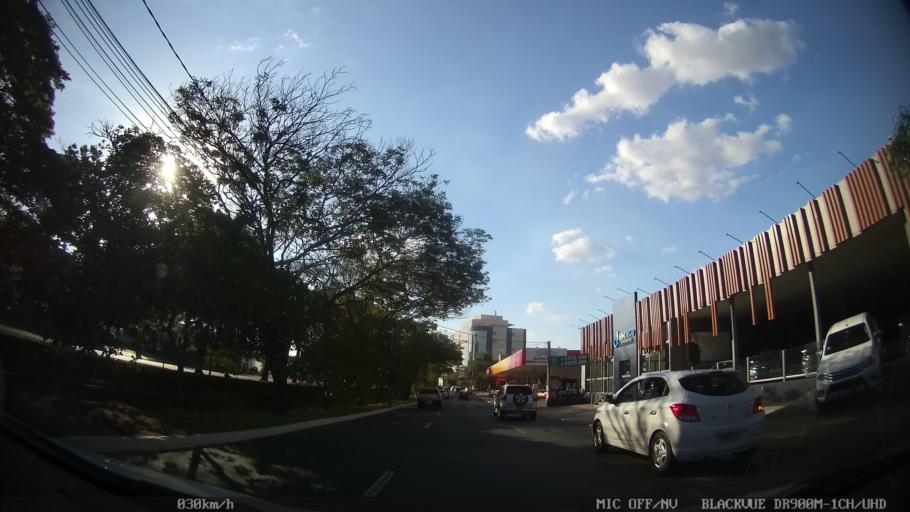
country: BR
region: Sao Paulo
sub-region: Ribeirao Preto
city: Ribeirao Preto
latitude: -21.1897
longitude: -47.7976
